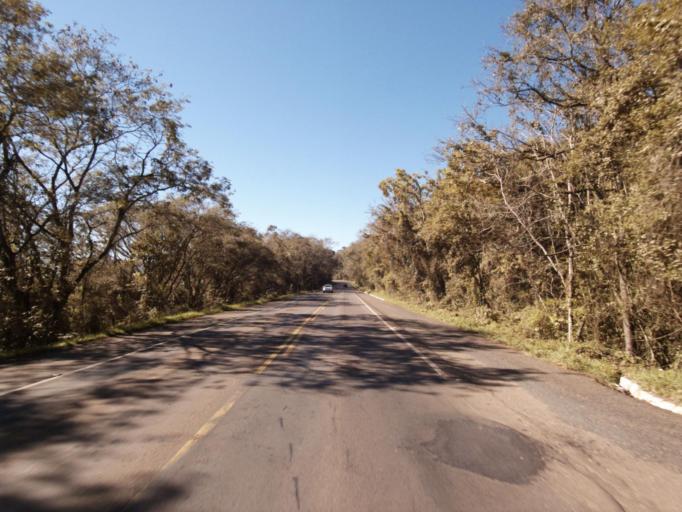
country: BR
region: Rio Grande do Sul
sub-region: Frederico Westphalen
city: Frederico Westphalen
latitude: -26.7984
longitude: -53.3401
